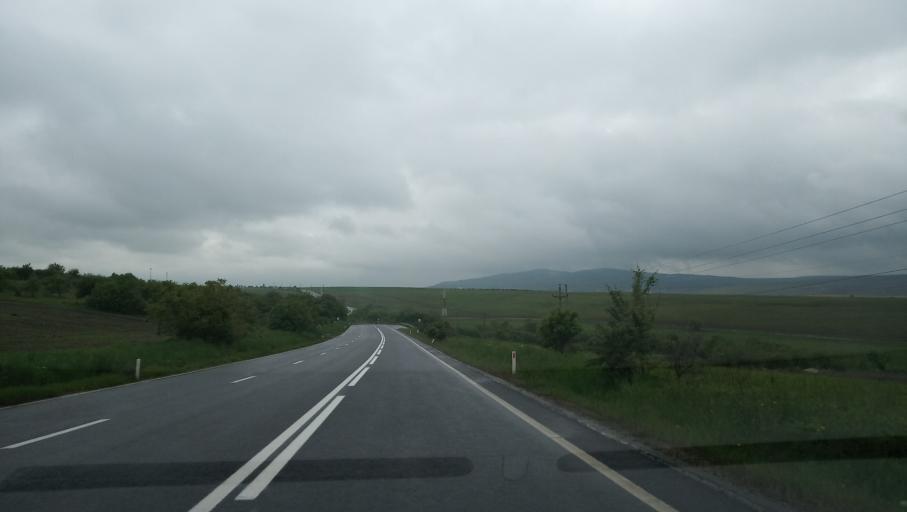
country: RO
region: Alba
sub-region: Comuna Cut
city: Cut
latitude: 45.9188
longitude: 23.7009
